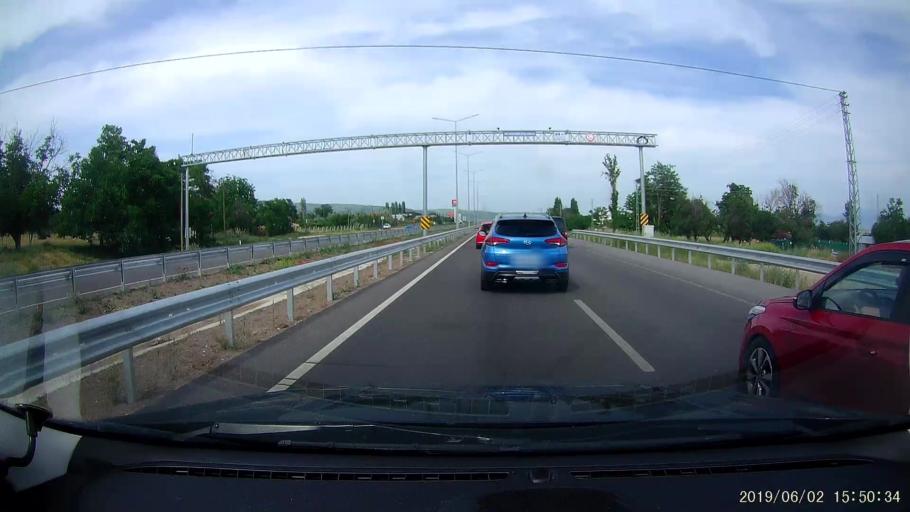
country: TR
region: Amasya
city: Merzifon
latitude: 40.8606
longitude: 35.4823
